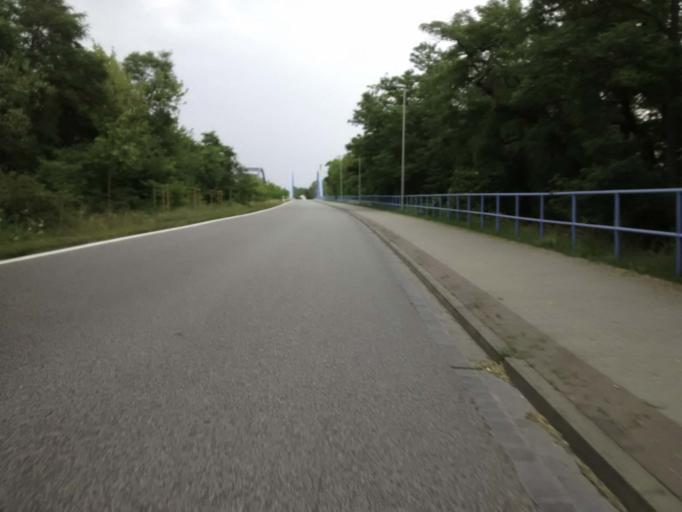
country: DE
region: Brandenburg
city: Wittenberge
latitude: 52.9861
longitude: 11.7617
